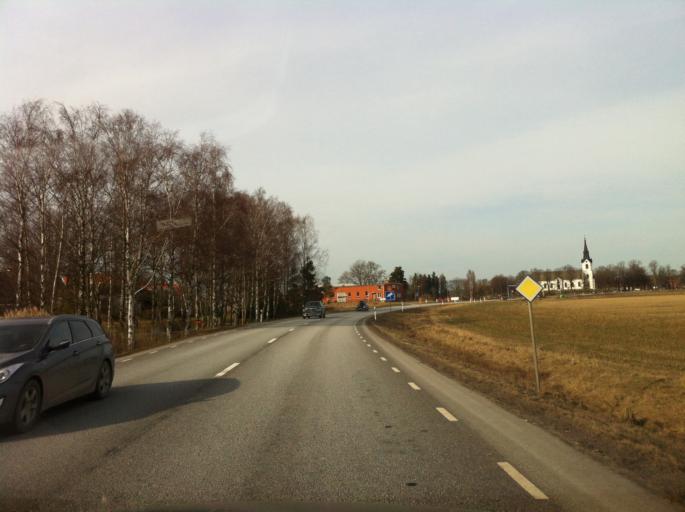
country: SE
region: Vaestra Goetaland
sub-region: Mariestads Kommun
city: Mariestad
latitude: 58.7494
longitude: 13.9449
